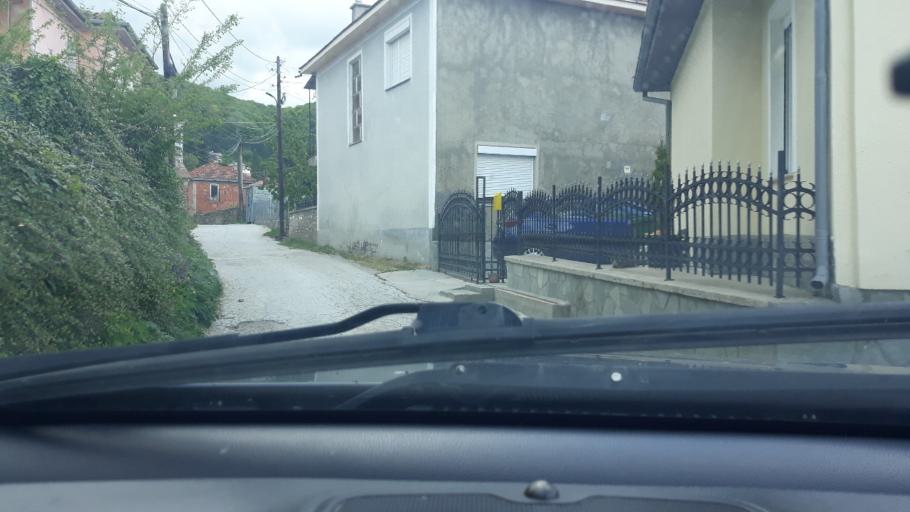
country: MK
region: Krusevo
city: Krushevo
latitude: 41.3671
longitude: 21.2533
